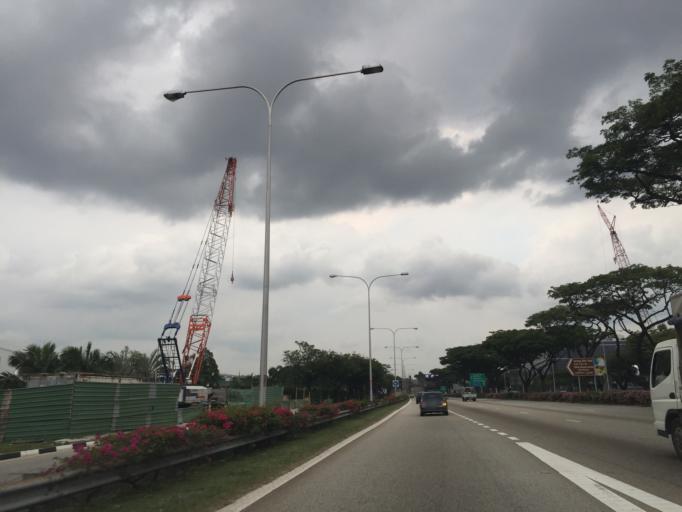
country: SG
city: Singapore
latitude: 1.3225
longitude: 103.7001
